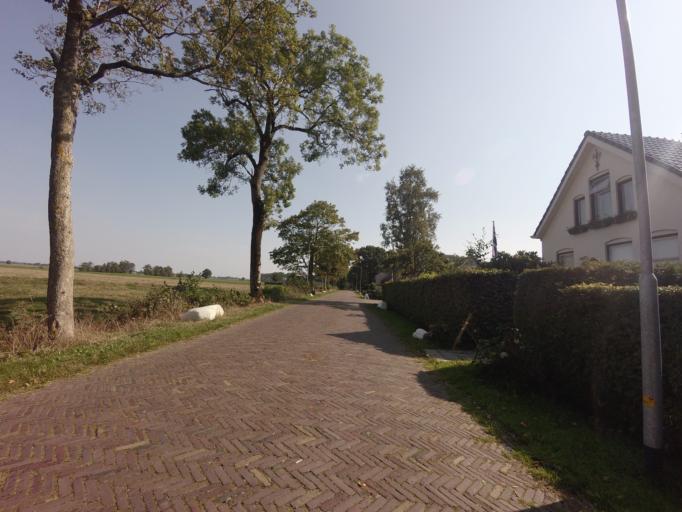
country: NL
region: Groningen
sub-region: Gemeente Zuidhorn
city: Zuidhorn
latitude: 53.2415
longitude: 6.4101
